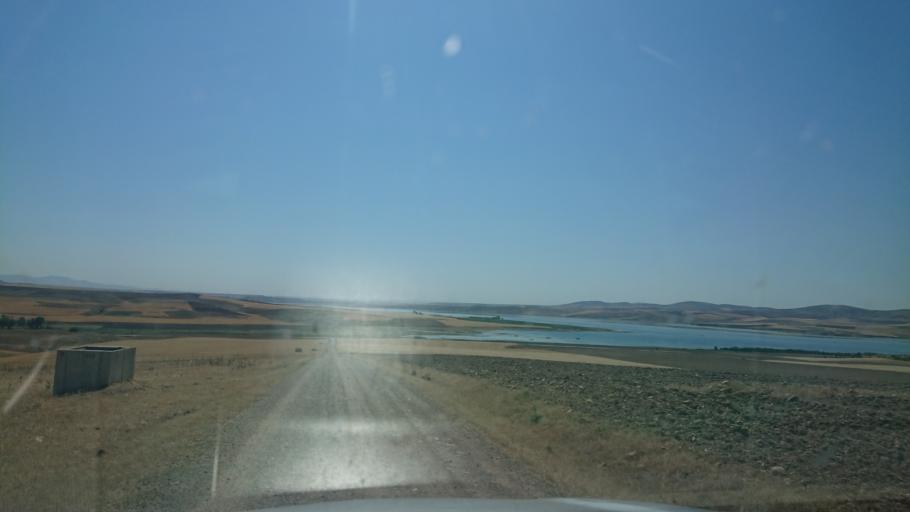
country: TR
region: Aksaray
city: Sariyahsi
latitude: 39.0561
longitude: 33.8902
